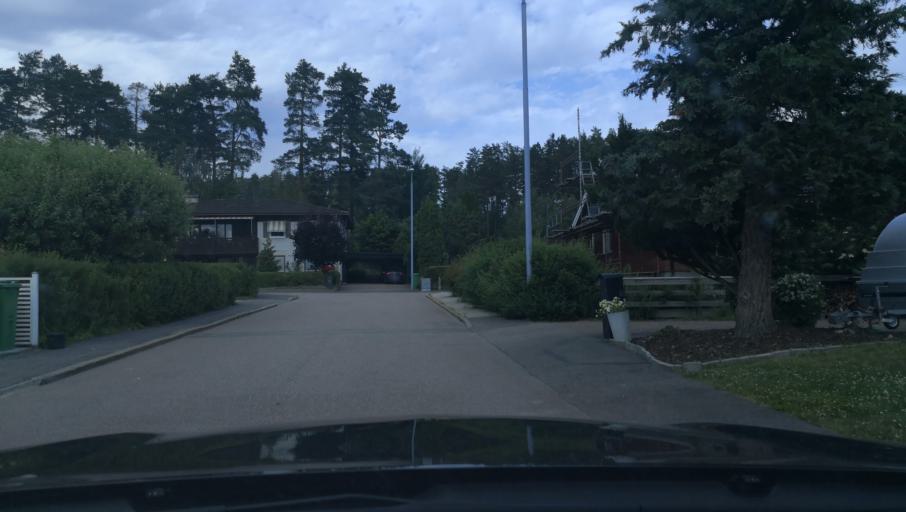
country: SE
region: Vaestmanland
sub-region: Fagersta Kommun
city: Fagersta
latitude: 59.9832
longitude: 15.8311
